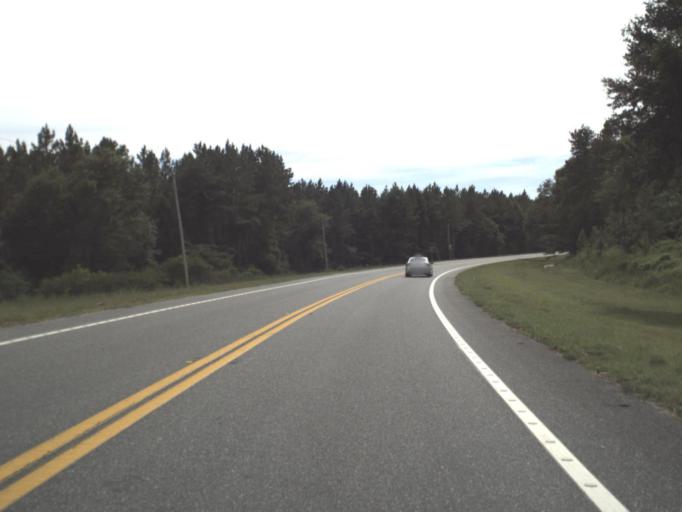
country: US
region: Florida
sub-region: Taylor County
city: Perry
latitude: 30.0819
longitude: -83.5026
